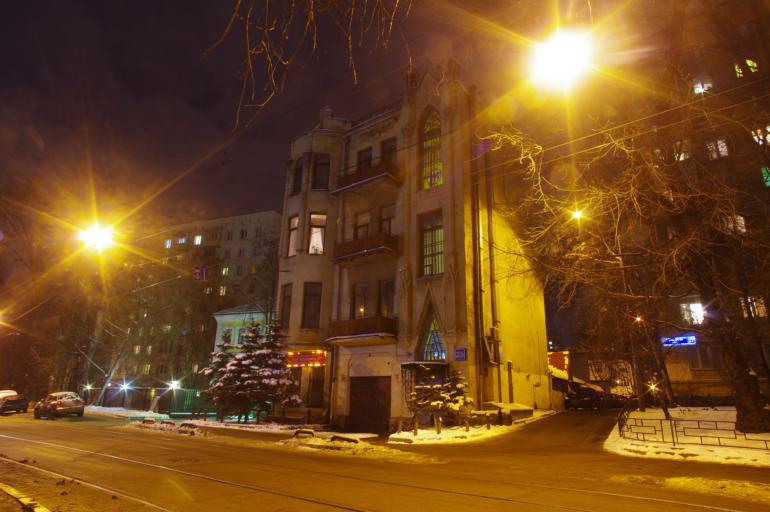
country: RU
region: Moscow
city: Lefortovo
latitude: 55.7742
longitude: 37.6781
